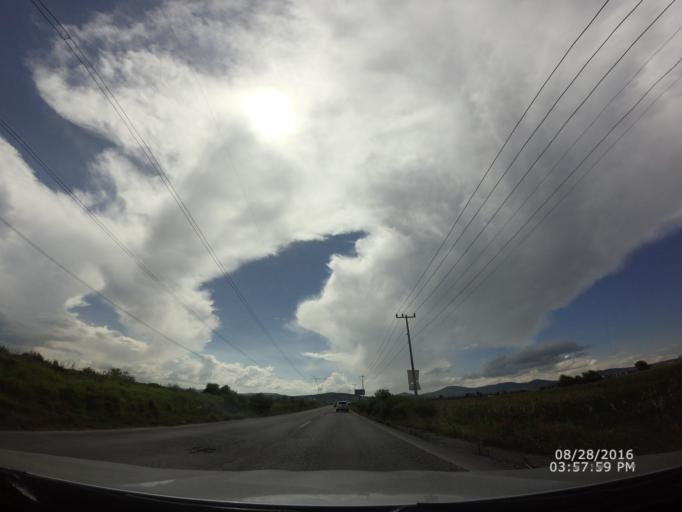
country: MX
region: Hidalgo
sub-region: Mineral de la Reforma
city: La Colonia
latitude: 20.0361
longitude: -98.7736
